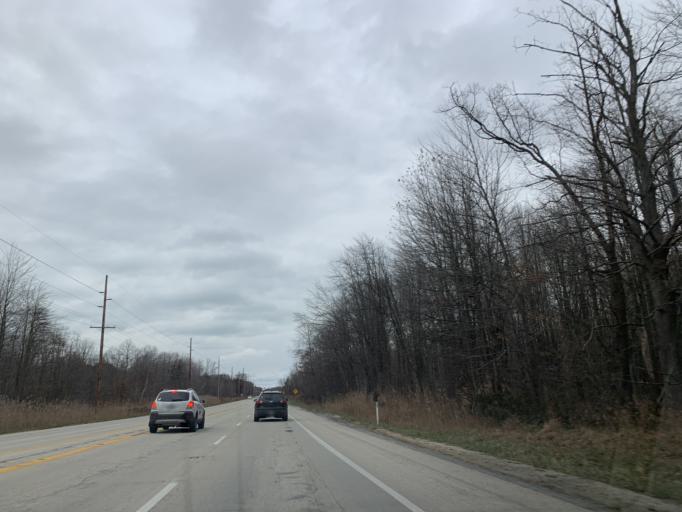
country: US
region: Indiana
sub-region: LaPorte County
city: Long Beach
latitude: 41.7261
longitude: -86.8261
